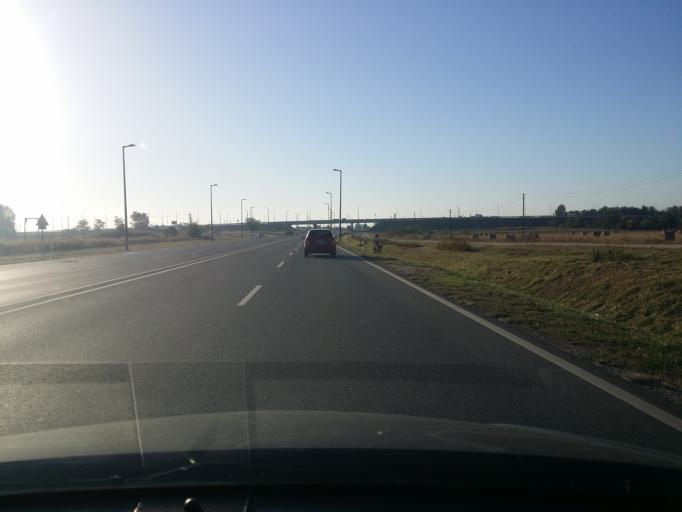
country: HU
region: Bacs-Kiskun
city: Kecskemet
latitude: 46.9439
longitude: 19.6555
